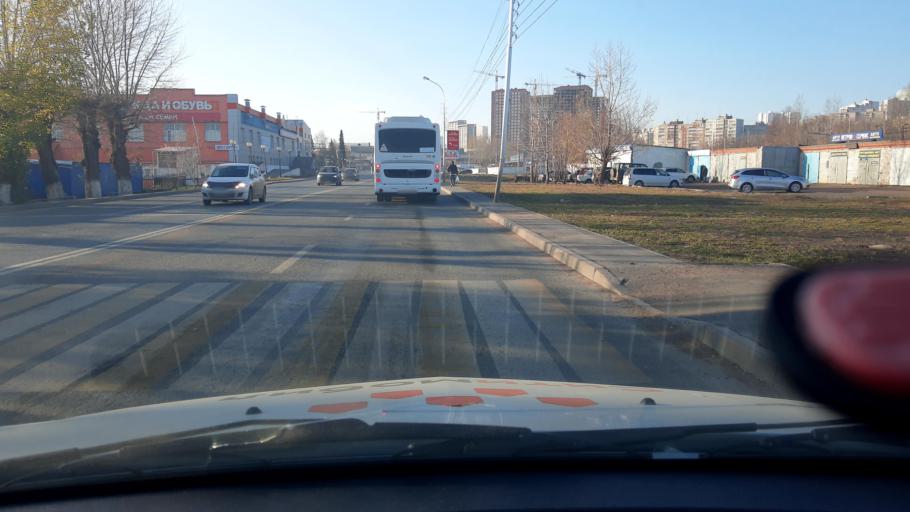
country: RU
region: Bashkortostan
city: Ufa
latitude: 54.7902
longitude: 56.0592
